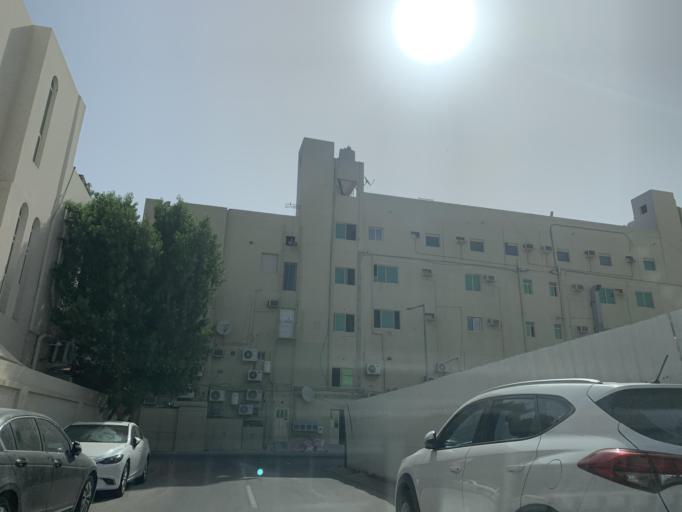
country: BH
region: Northern
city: Ar Rifa'
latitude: 26.1469
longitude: 50.5839
